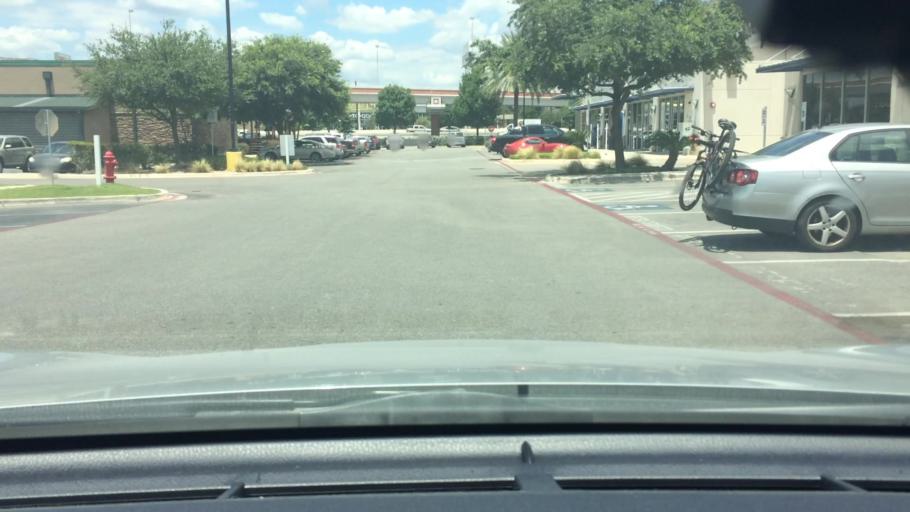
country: US
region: Texas
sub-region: Bexar County
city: Castle Hills
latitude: 29.5192
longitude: -98.5035
